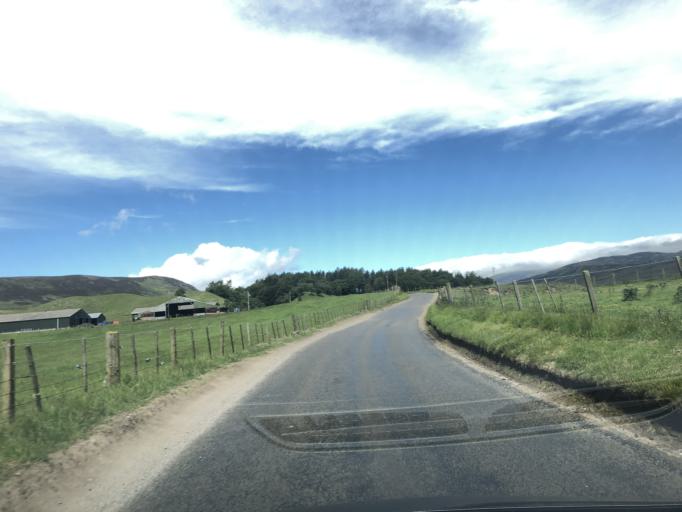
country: GB
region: Scotland
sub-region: Angus
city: Kirriemuir
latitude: 56.7593
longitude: -3.0185
